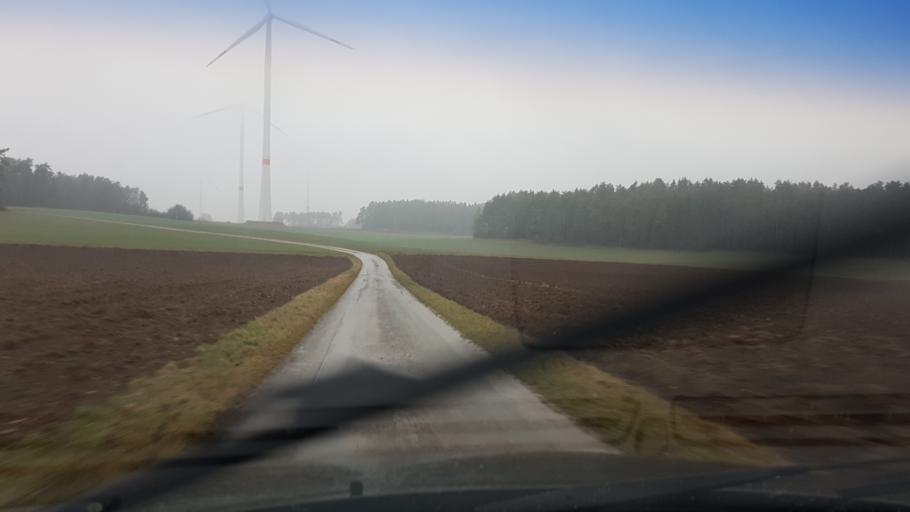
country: DE
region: Bavaria
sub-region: Upper Franconia
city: Kasendorf
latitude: 50.0357
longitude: 11.3054
